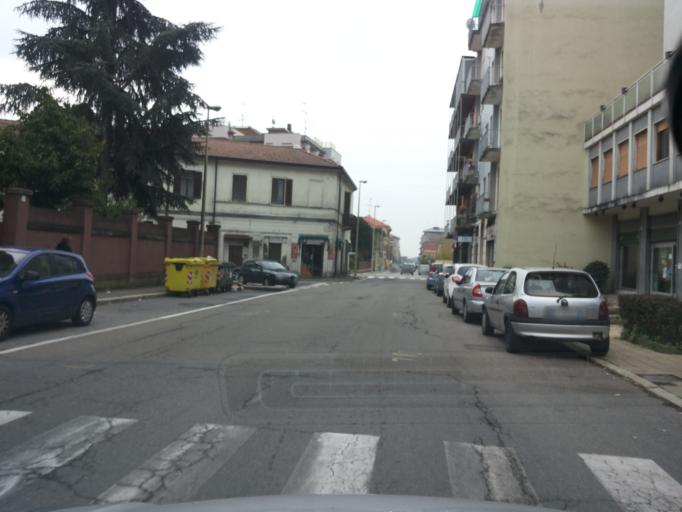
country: IT
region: Piedmont
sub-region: Provincia di Vercelli
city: Vercelli
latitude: 45.3209
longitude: 8.4264
